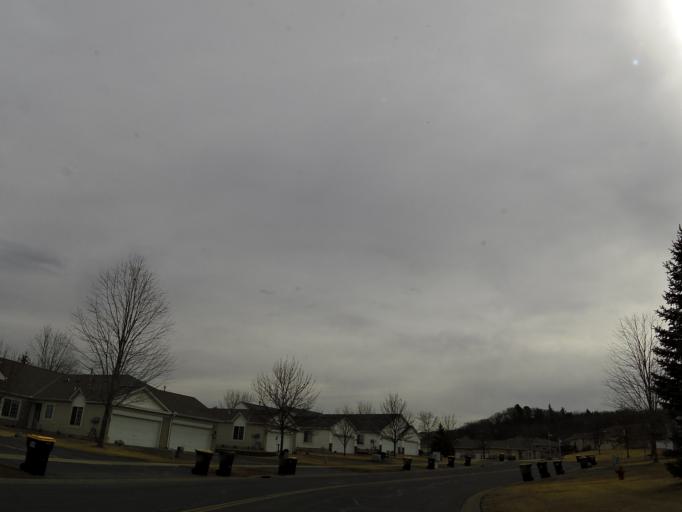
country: US
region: Minnesota
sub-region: Scott County
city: Savage
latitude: 44.7671
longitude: -93.3923
